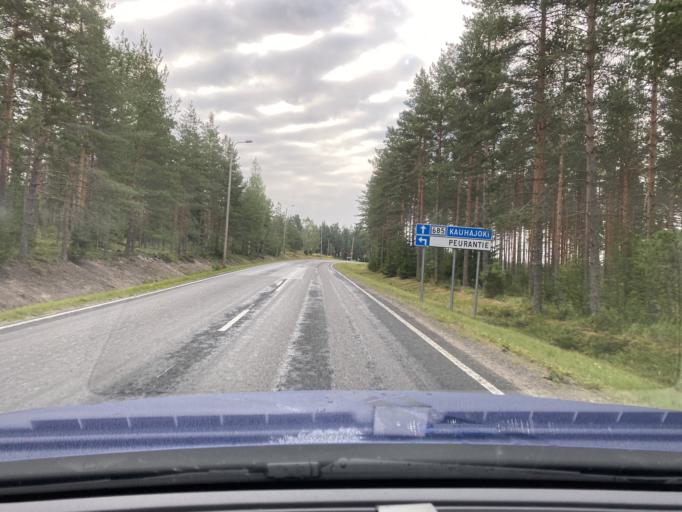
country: FI
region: Southern Ostrobothnia
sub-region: Seinaejoki
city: Jurva
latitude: 62.6776
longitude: 21.9791
